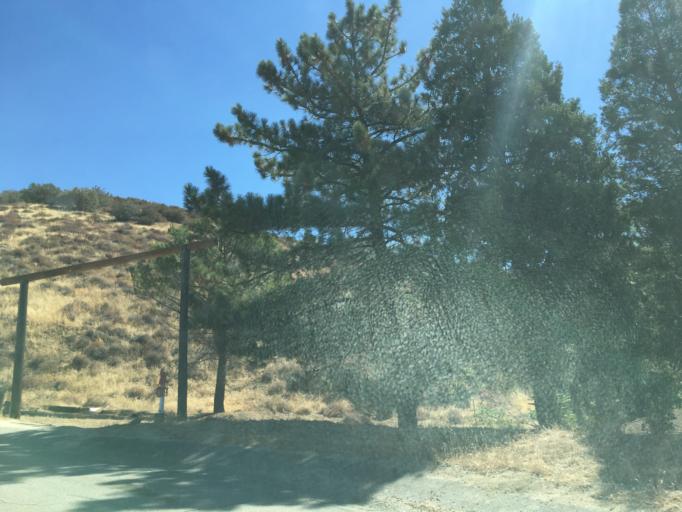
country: US
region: California
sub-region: Los Angeles County
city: Green Valley
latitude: 34.6778
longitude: -118.4465
